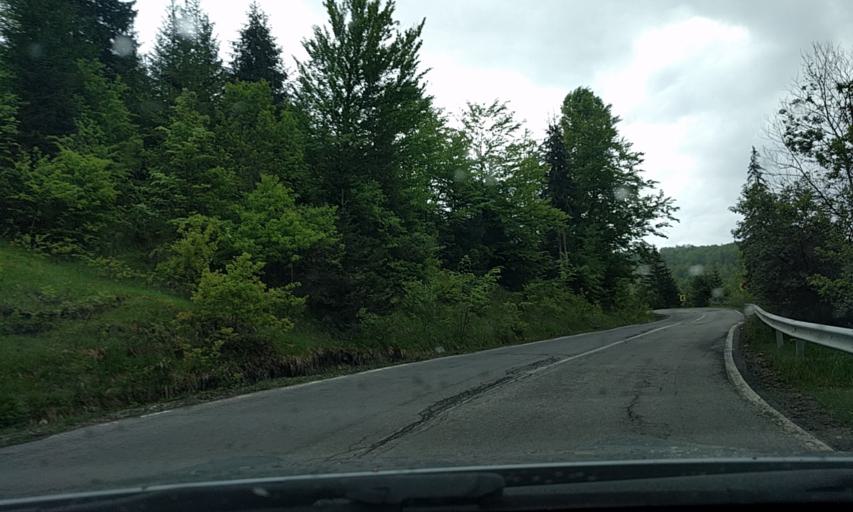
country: RO
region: Prahova
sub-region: Oras Sinaia
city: Sinaia
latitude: 45.3015
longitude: 25.5135
